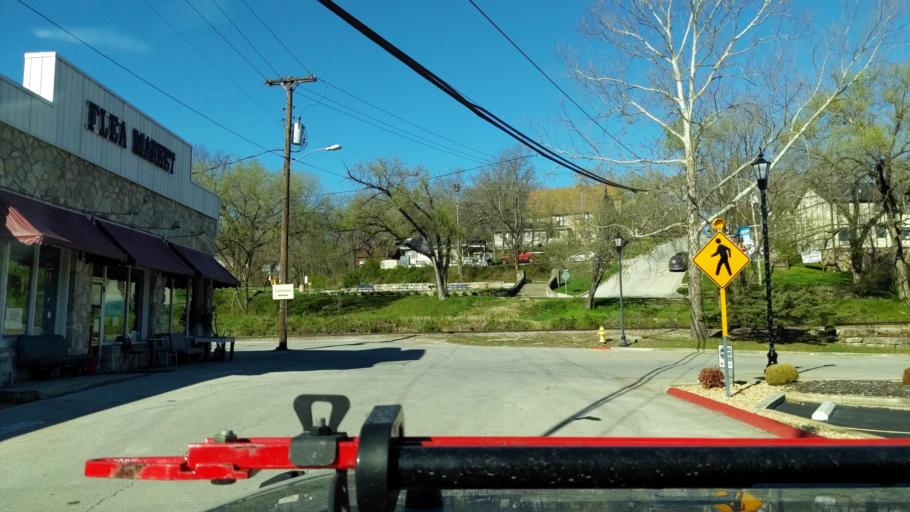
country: US
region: Missouri
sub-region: Taney County
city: Hollister
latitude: 36.6225
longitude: -93.2154
